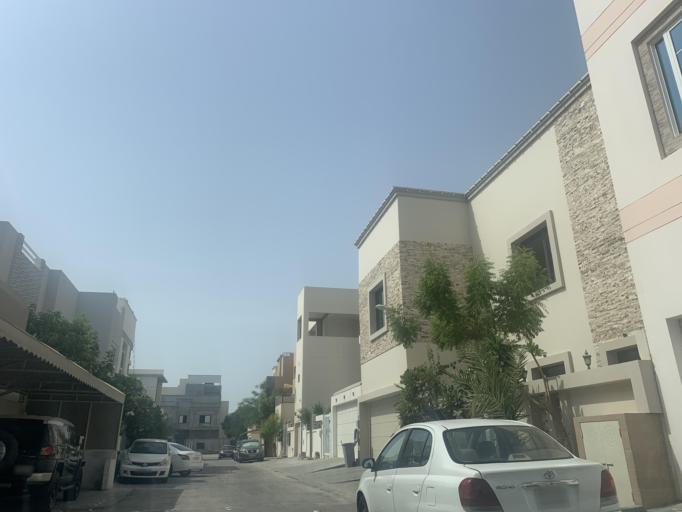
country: BH
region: Manama
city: Jidd Hafs
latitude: 26.2062
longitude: 50.4674
